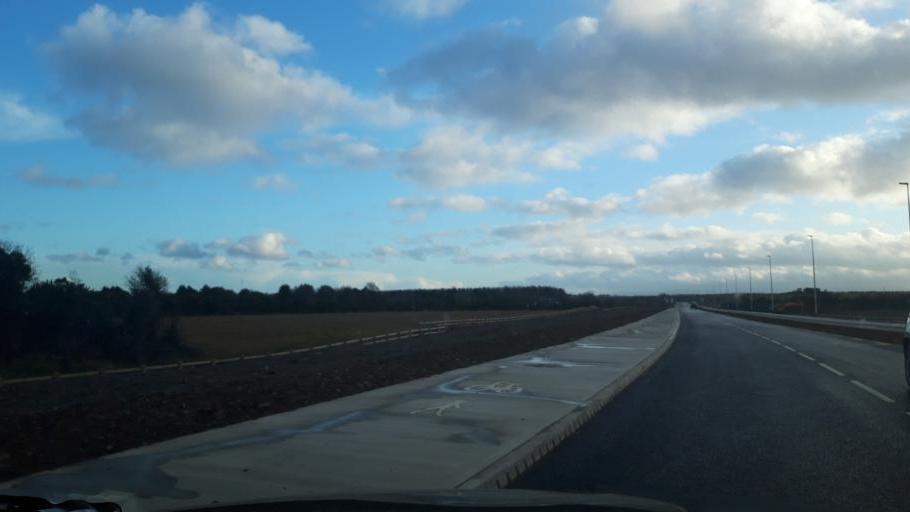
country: IE
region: Leinster
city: Donabate
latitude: 53.4873
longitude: -6.1363
